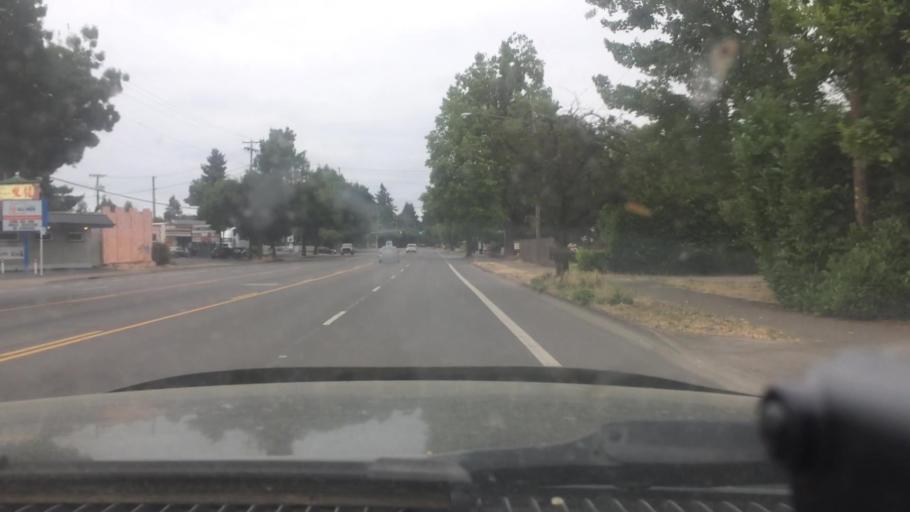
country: US
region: Oregon
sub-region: Lane County
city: Eugene
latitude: 44.0775
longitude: -123.1205
